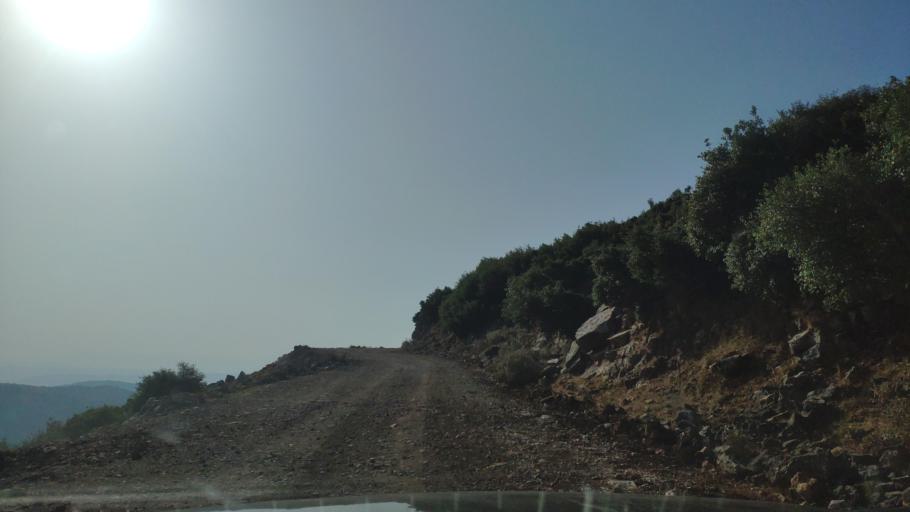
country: GR
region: West Greece
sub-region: Nomos Aitolias kai Akarnanias
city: Monastirakion
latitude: 38.8382
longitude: 20.9778
